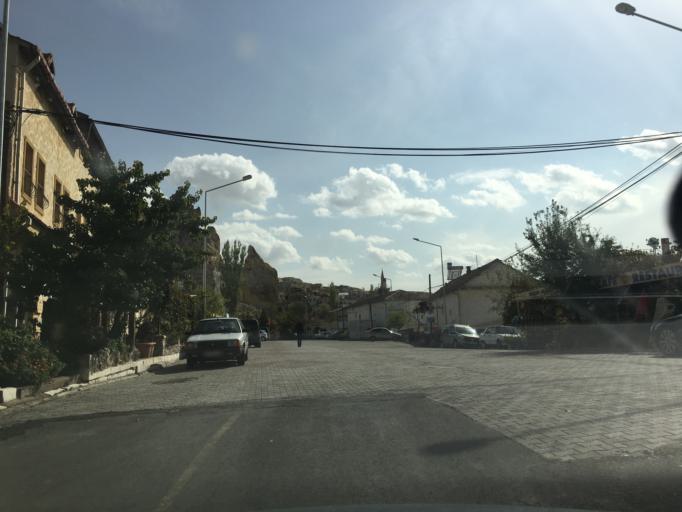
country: TR
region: Nevsehir
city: Goereme
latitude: 38.6697
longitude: 34.8409
